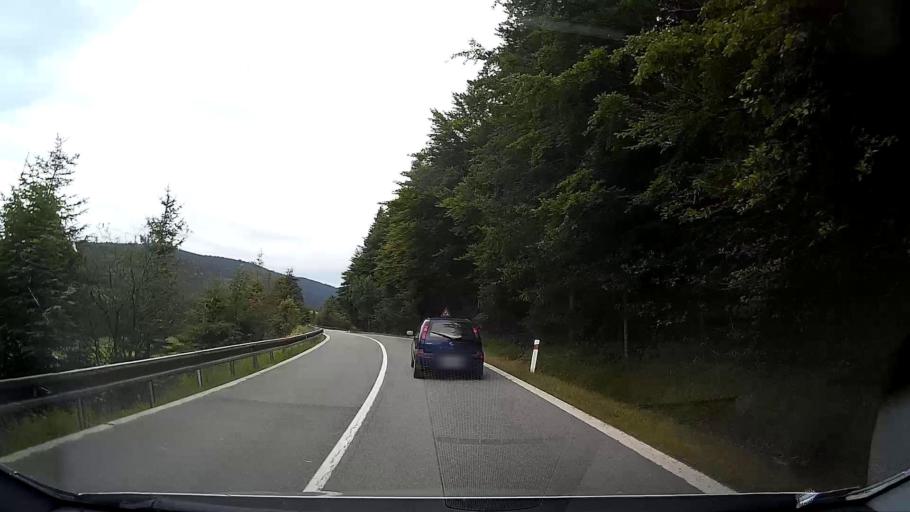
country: SK
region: Kosicky
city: Dobsina
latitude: 48.8698
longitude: 20.2250
